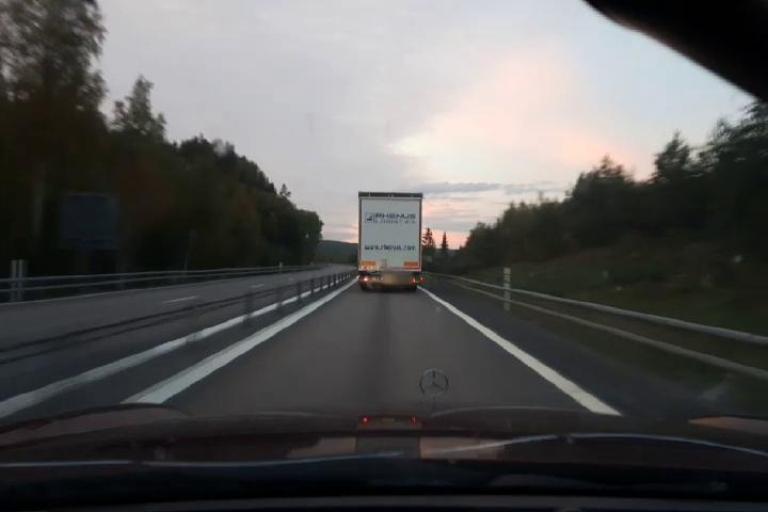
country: SE
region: Vaesternorrland
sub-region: Haernoesands Kommun
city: Haernoesand
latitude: 62.8240
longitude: 17.9700
